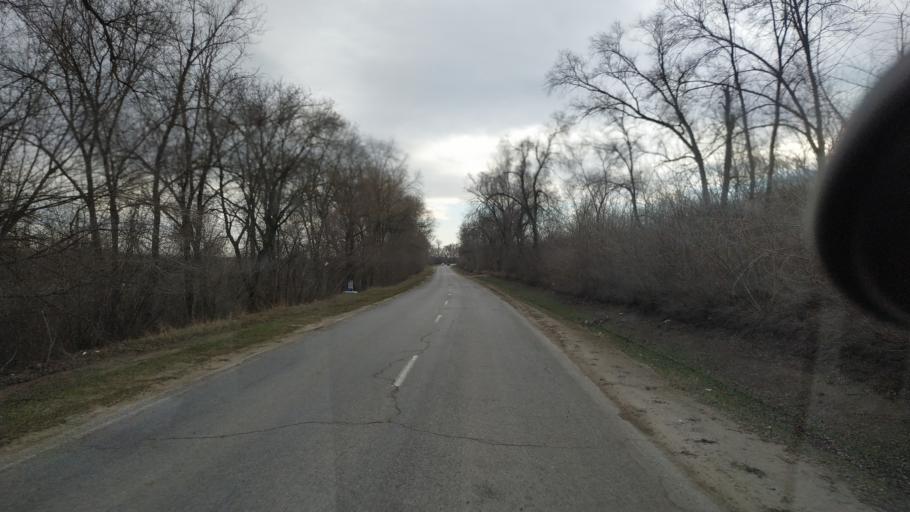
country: MD
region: Chisinau
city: Vadul lui Voda
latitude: 47.1294
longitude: 29.0624
